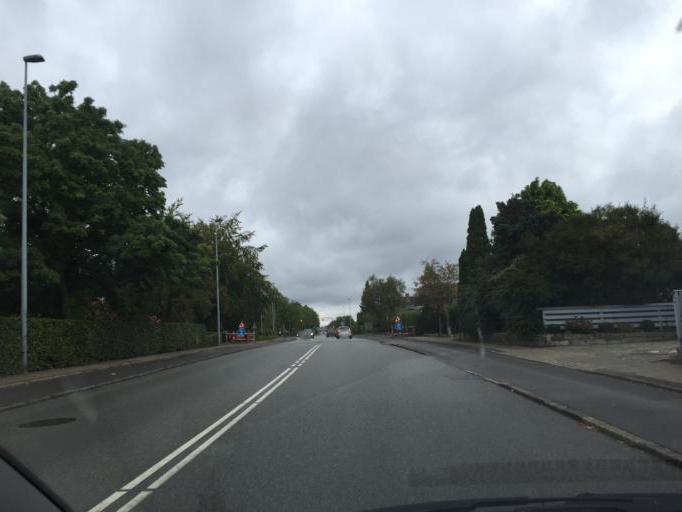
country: DK
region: Capital Region
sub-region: Gladsaxe Municipality
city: Buddinge
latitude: 55.7428
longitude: 12.4724
